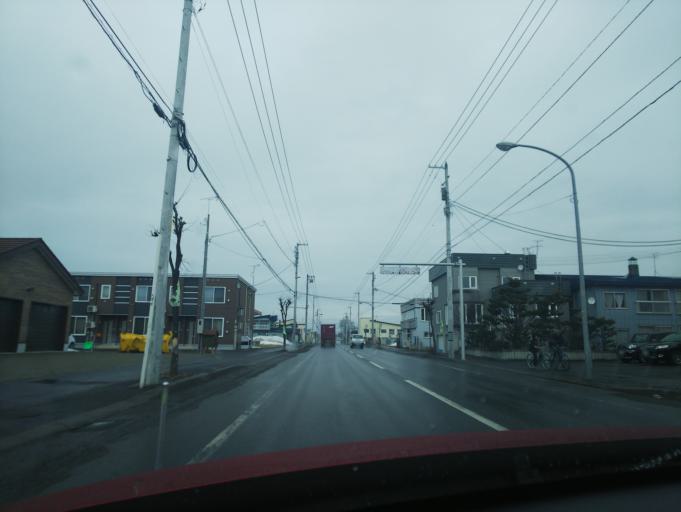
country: JP
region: Hokkaido
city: Nayoro
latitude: 44.3416
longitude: 142.4642
